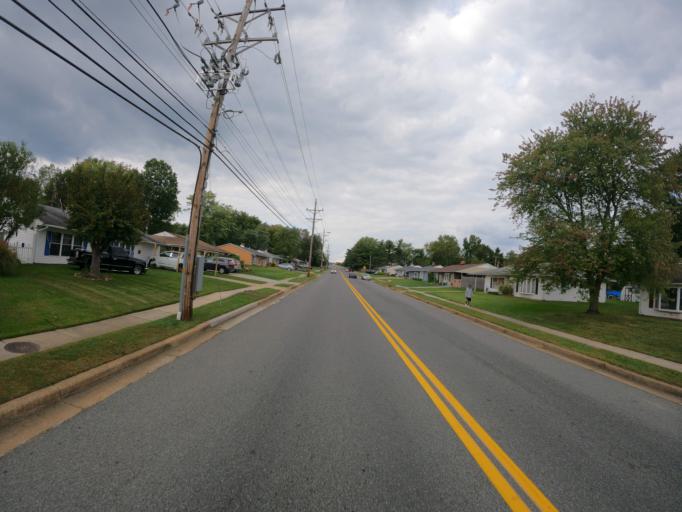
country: US
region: Delaware
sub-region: New Castle County
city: Brookside
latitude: 39.6719
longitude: -75.7279
